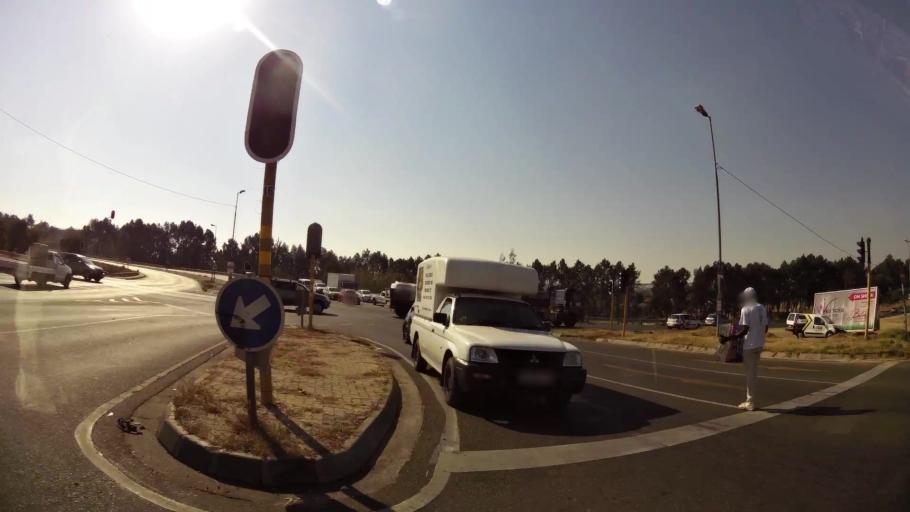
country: ZA
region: Gauteng
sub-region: City of Johannesburg Metropolitan Municipality
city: Modderfontein
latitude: -26.1099
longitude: 28.1499
